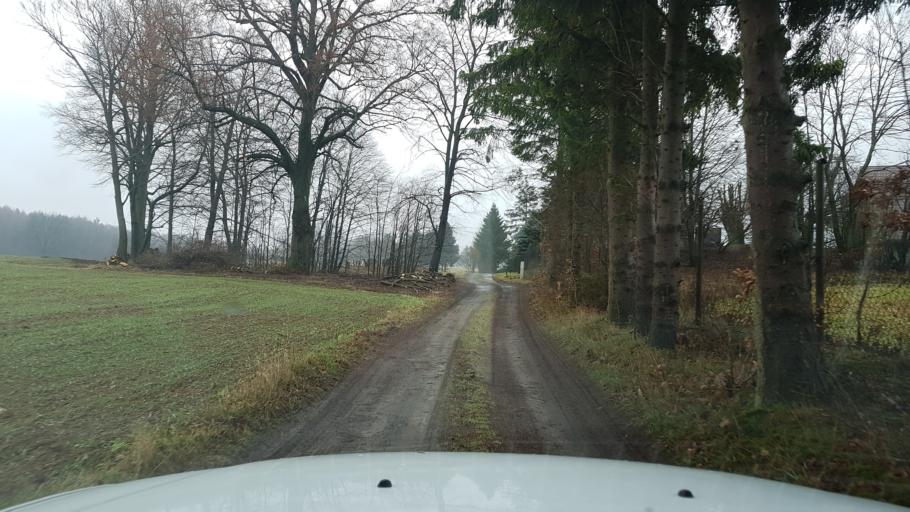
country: PL
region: West Pomeranian Voivodeship
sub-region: Powiat drawski
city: Czaplinek
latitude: 53.5777
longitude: 16.2653
